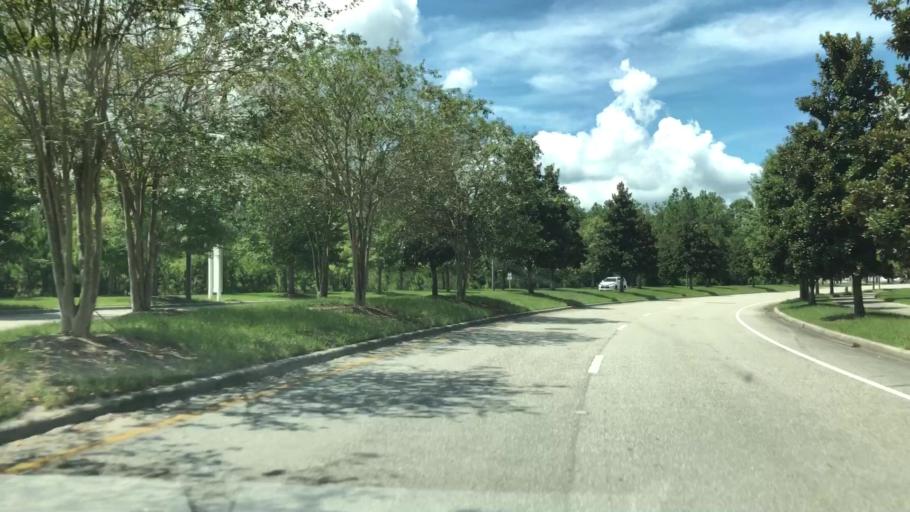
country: US
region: Florida
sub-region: Saint Johns County
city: Palm Valley
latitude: 30.1052
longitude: -81.4377
